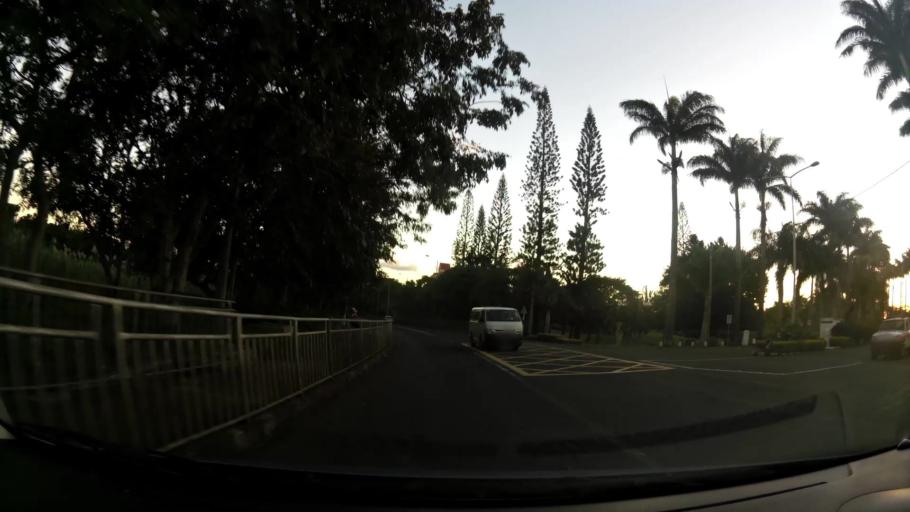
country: MU
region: Moka
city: Moka
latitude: -20.2267
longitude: 57.5056
